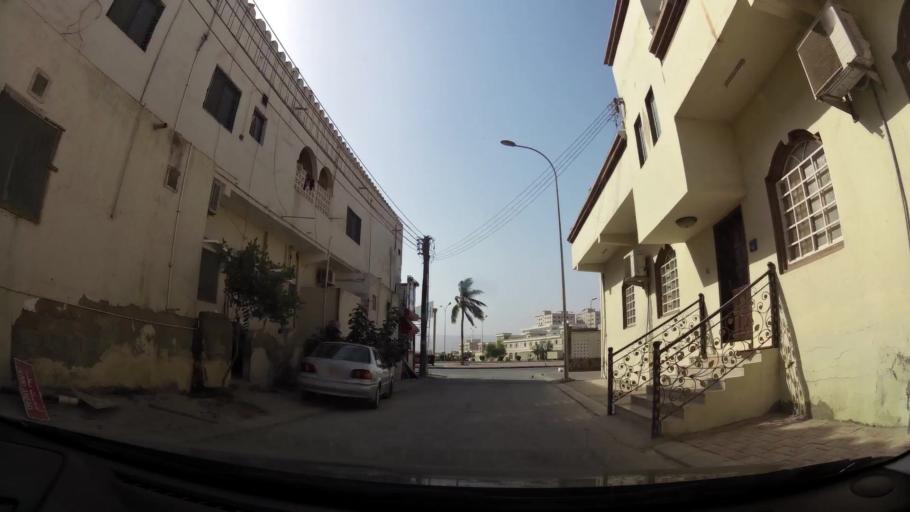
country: OM
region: Zufar
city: Salalah
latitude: 17.0019
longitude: 54.0388
